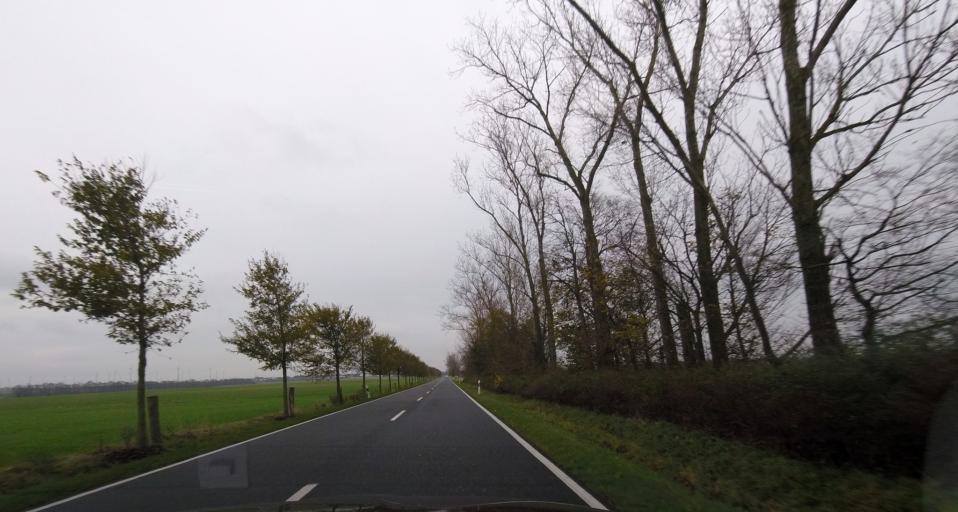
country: DE
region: Saxony-Anhalt
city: Kropstadt
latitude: 52.0122
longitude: 12.7592
